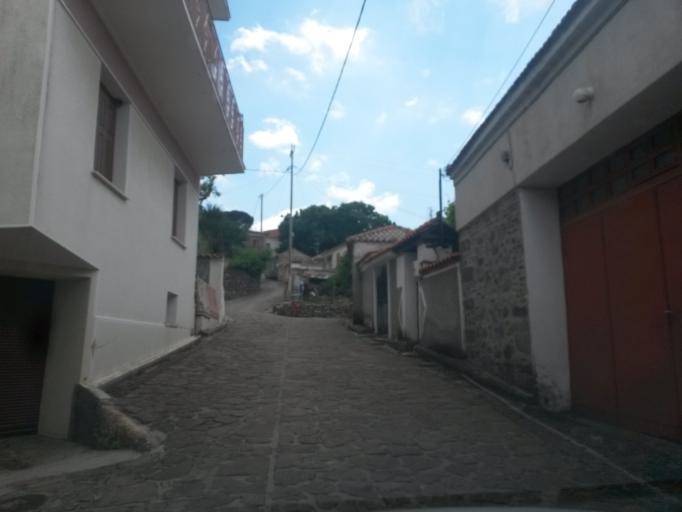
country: GR
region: North Aegean
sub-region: Nomos Lesvou
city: Eresos
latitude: 39.2261
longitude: 26.0495
